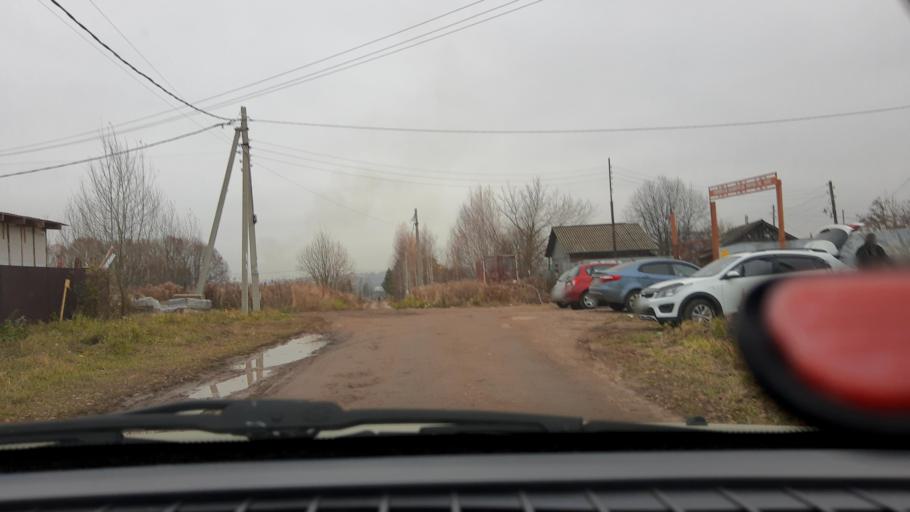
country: RU
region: Nizjnij Novgorod
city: Afonino
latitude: 56.2562
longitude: 44.0580
